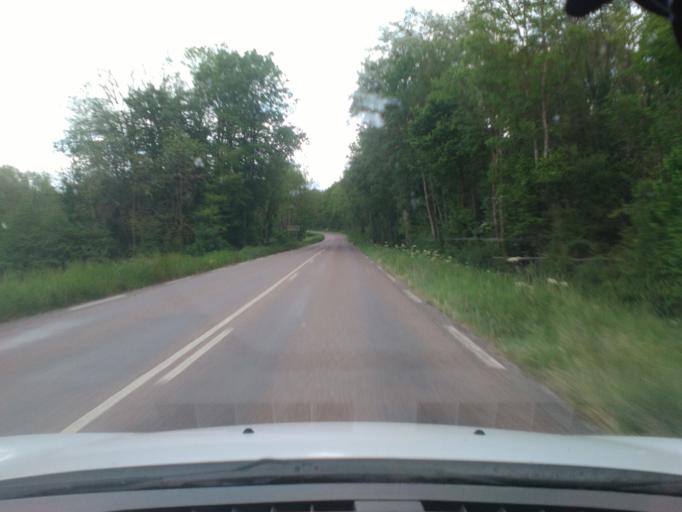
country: FR
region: Lorraine
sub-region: Departement des Vosges
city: Mirecourt
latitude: 48.3062
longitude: 6.0704
